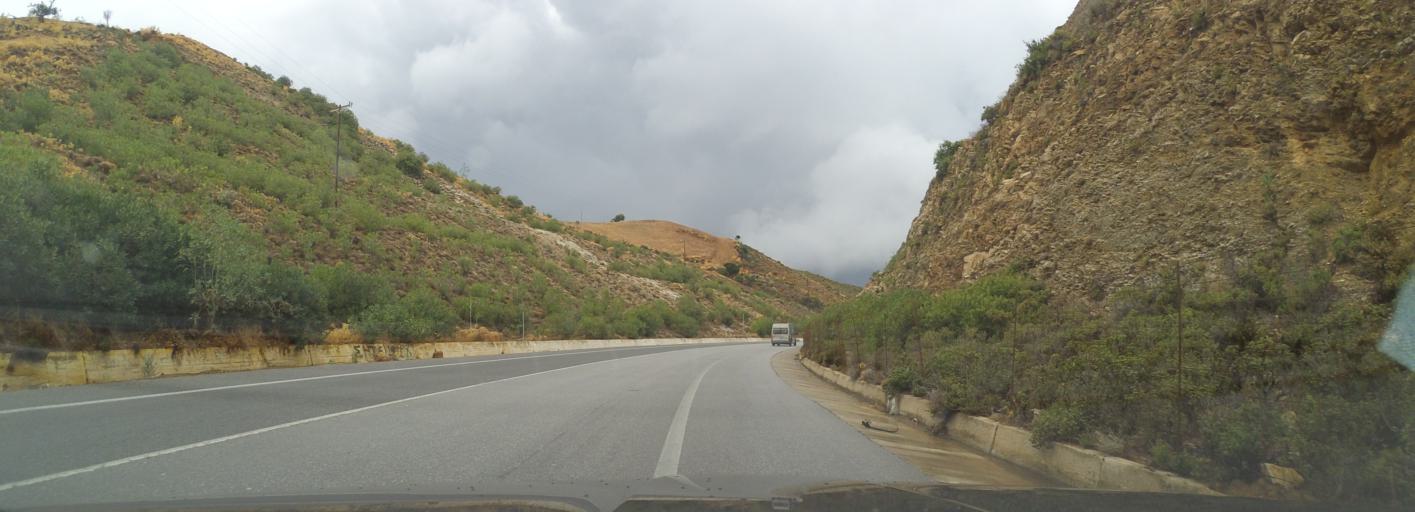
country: GR
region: Crete
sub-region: Nomos Rethymnis
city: Anogeia
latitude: 35.3902
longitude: 24.9301
